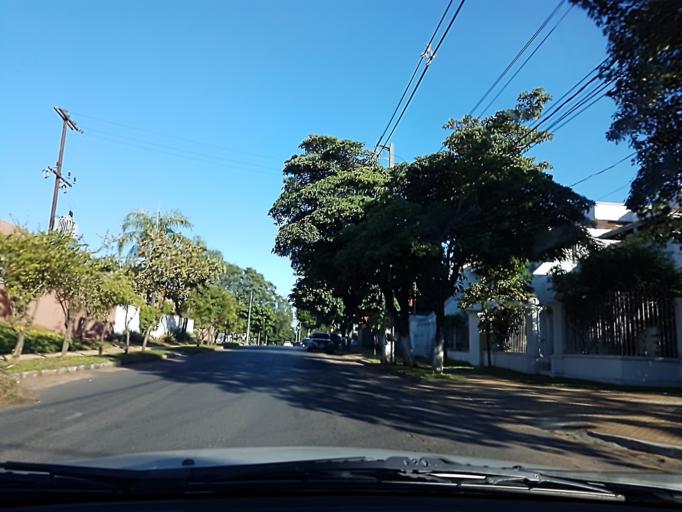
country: PY
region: Asuncion
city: Asuncion
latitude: -25.2793
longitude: -57.5826
